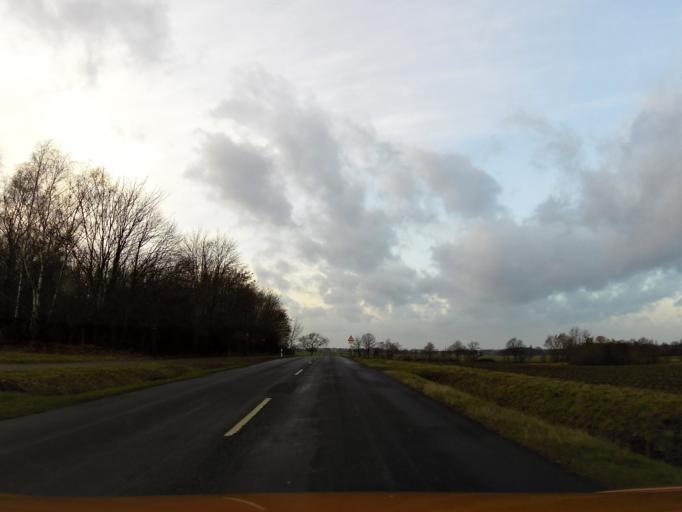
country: DE
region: Lower Saxony
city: Gross Twulpstedt
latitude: 52.3838
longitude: 10.8825
